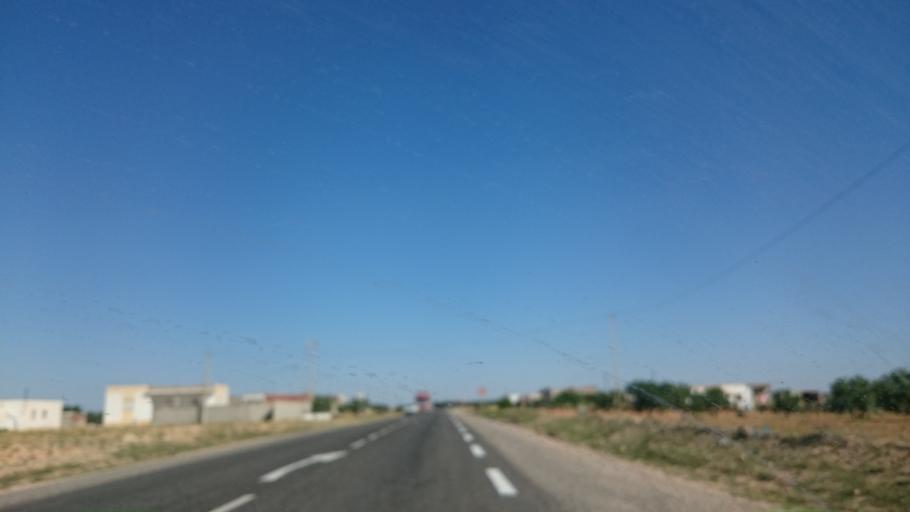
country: TN
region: Safaqis
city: Sfax
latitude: 34.7833
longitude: 10.5024
